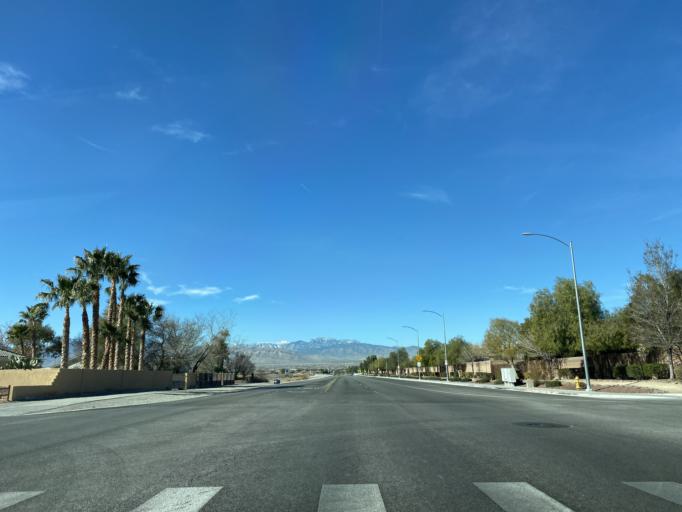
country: US
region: Nevada
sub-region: Clark County
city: North Las Vegas
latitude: 36.3050
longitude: -115.2284
